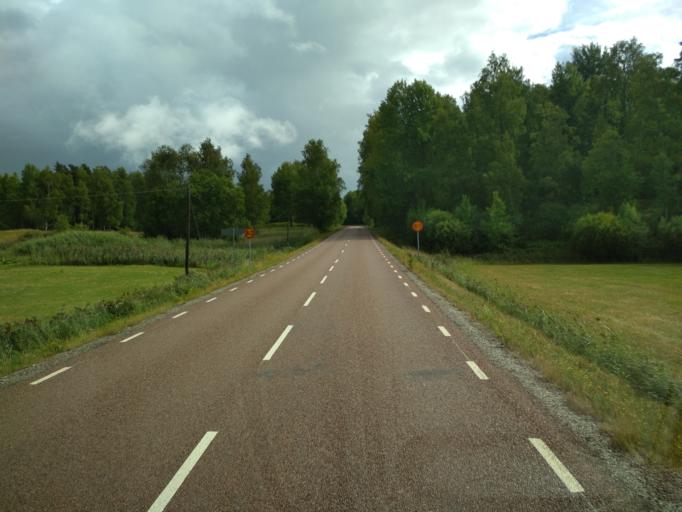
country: SE
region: Vaestmanland
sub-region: Surahammars Kommun
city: Ramnas
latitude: 59.8673
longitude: 16.0863
